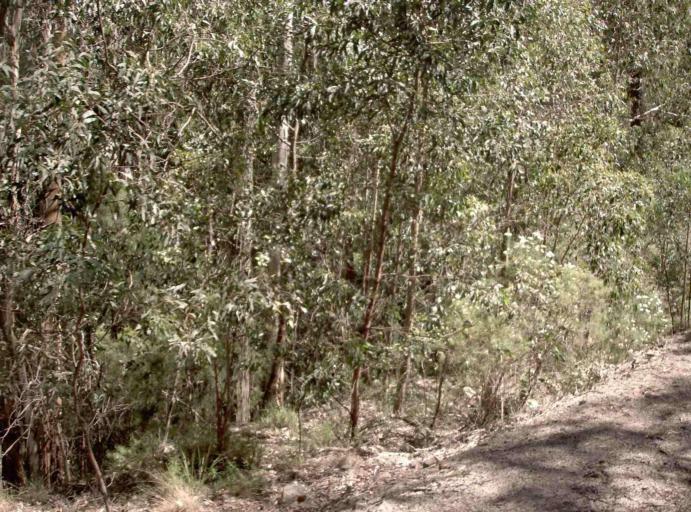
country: AU
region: Victoria
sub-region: East Gippsland
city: Lakes Entrance
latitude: -37.3805
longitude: 148.2192
